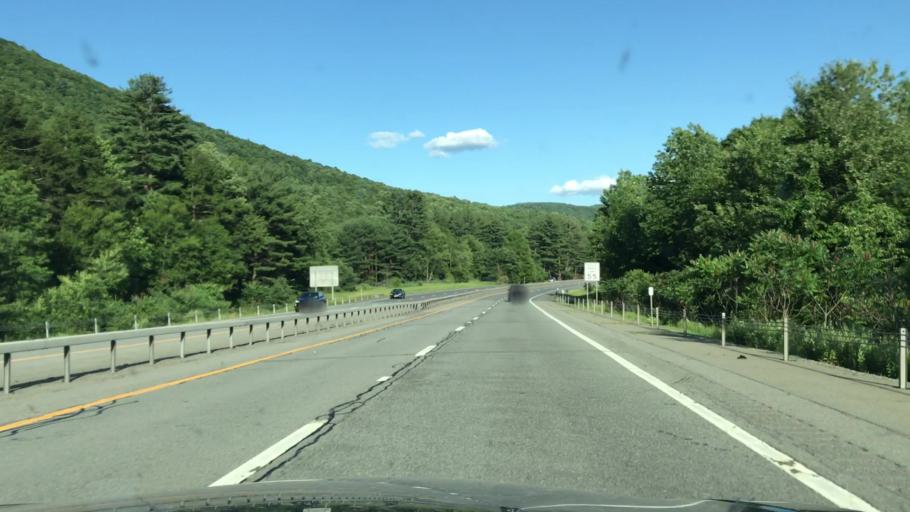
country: US
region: New York
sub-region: Delaware County
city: Hancock
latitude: 41.9872
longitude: -75.1187
